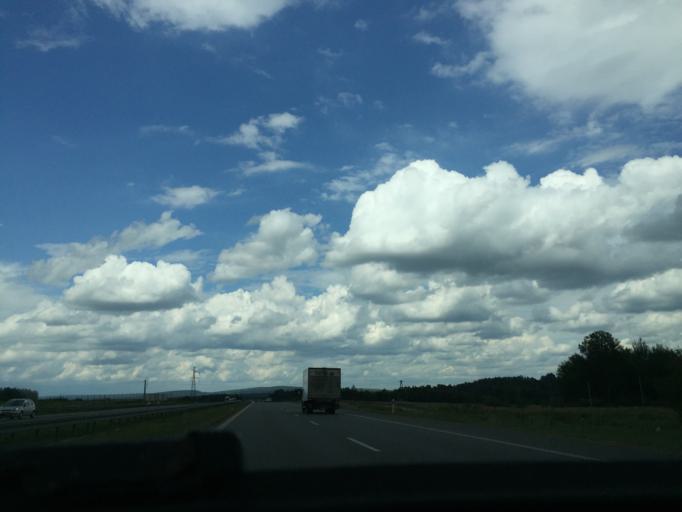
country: PL
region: Swietokrzyskie
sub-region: Powiat kielecki
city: Piekoszow
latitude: 50.8698
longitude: 20.5160
